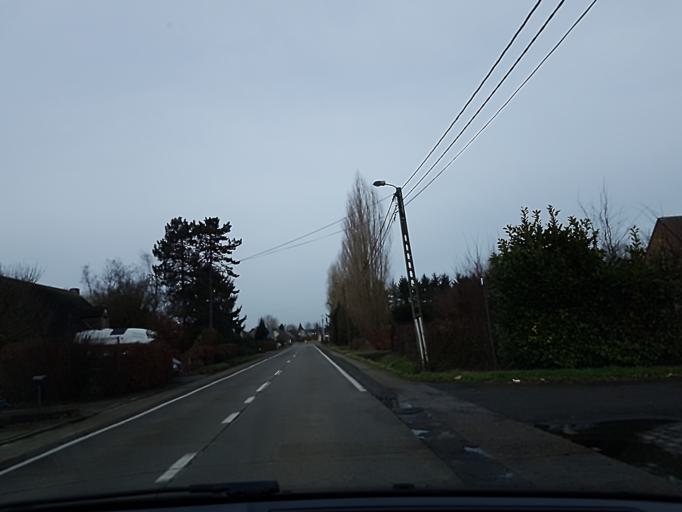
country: BE
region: Flanders
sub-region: Provincie Antwerpen
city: Putte
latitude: 51.0841
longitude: 4.6166
